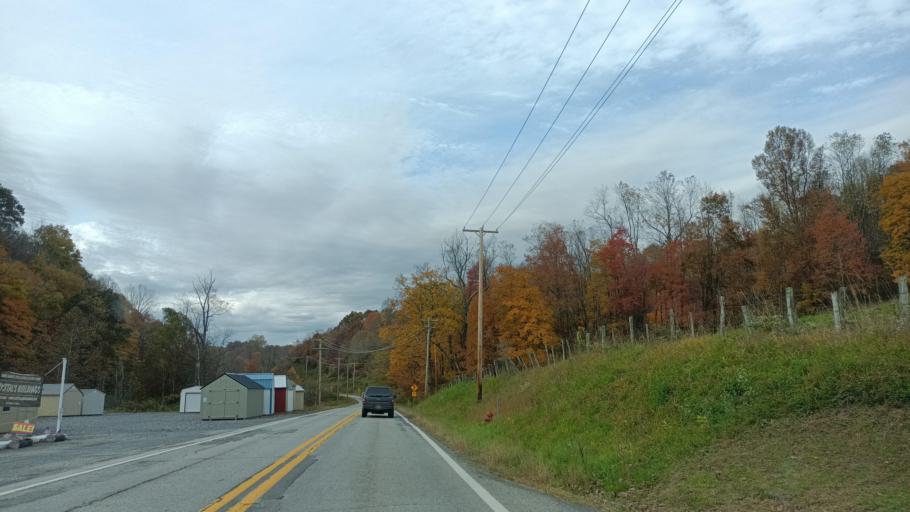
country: US
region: West Virginia
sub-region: Taylor County
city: Grafton
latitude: 39.3347
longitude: -79.8502
